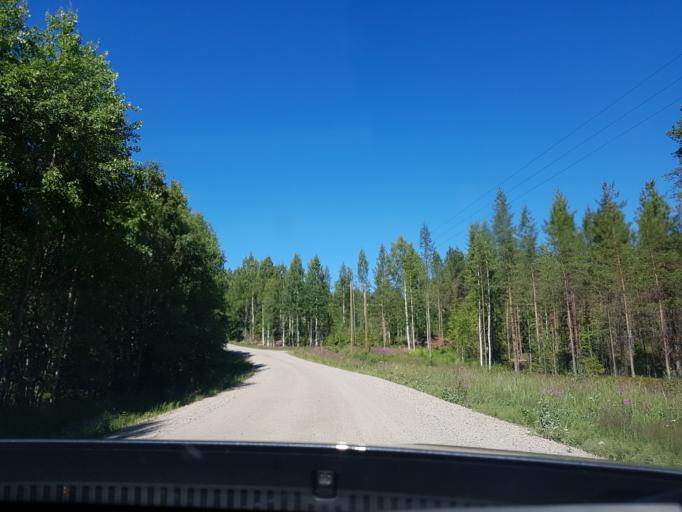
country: FI
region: Kainuu
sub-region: Kehys-Kainuu
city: Kuhmo
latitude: 64.1753
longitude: 29.6324
